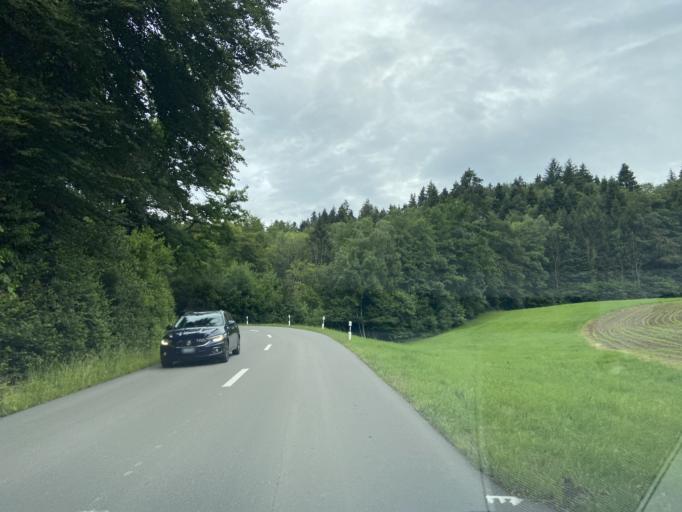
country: CH
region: Thurgau
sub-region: Muenchwilen District
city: Aadorf
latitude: 47.4663
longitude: 8.8916
